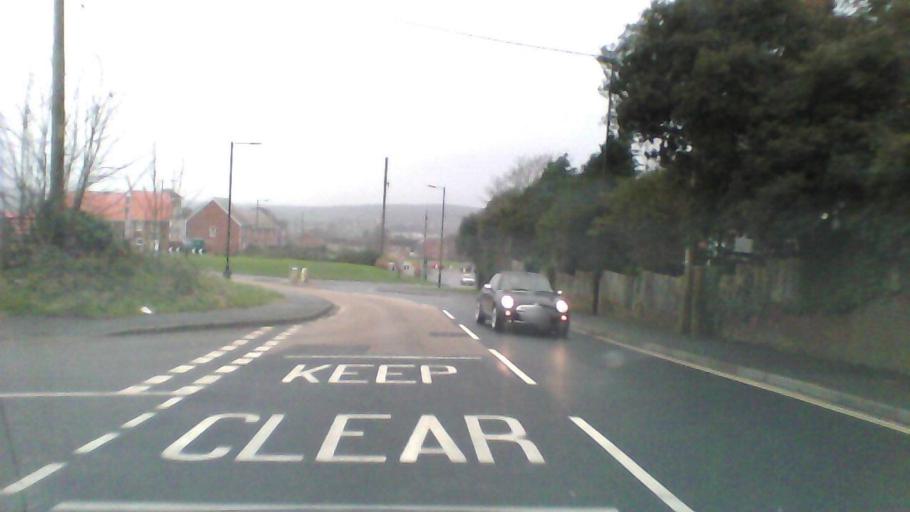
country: GB
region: England
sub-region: Isle of Wight
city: Newport
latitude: 50.7005
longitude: -1.2745
